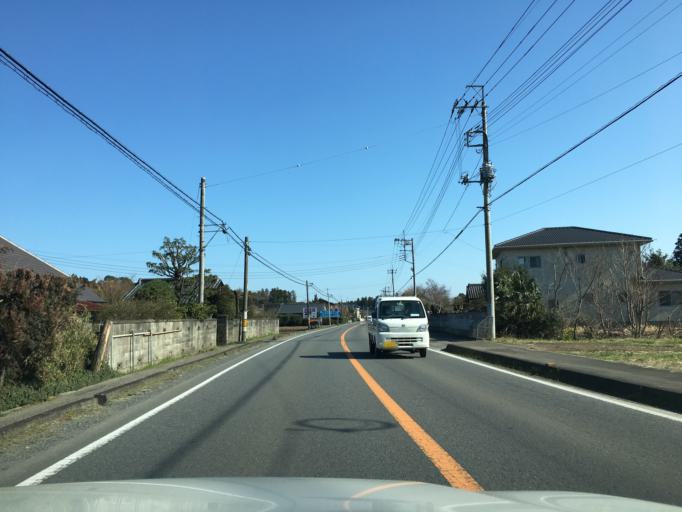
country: JP
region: Ibaraki
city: Omiya
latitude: 36.4713
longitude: 140.3927
